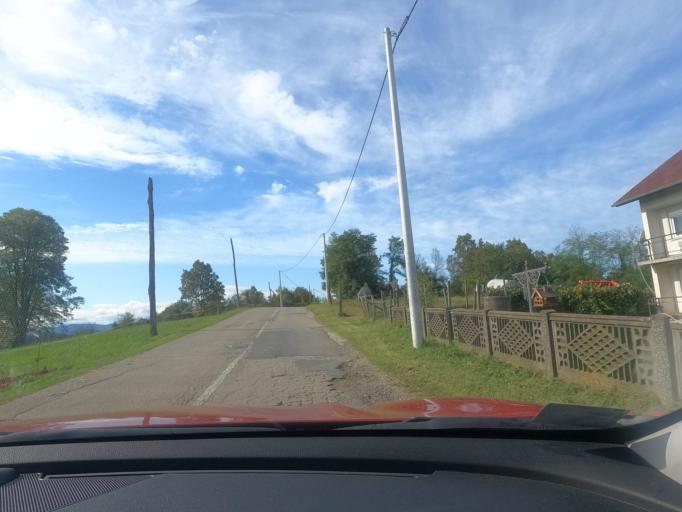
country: HR
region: Sisacko-Moslavacka
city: Glina
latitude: 45.3006
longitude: 16.1678
